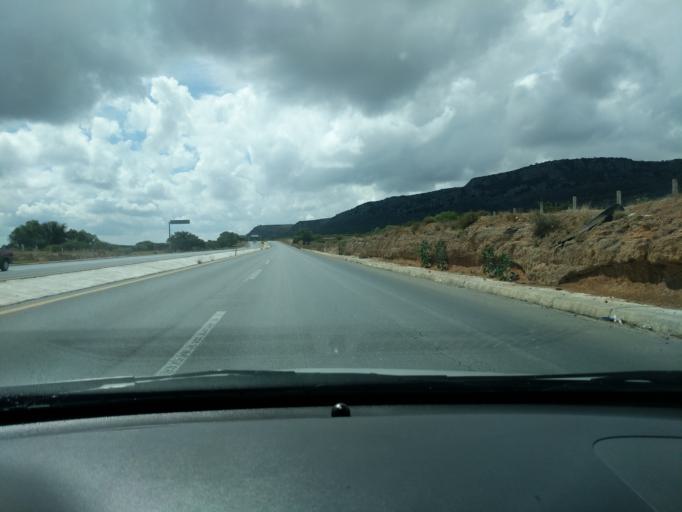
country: MX
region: Zacatecas
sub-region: Pinos
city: Santiago
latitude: 22.4038
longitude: -101.3853
